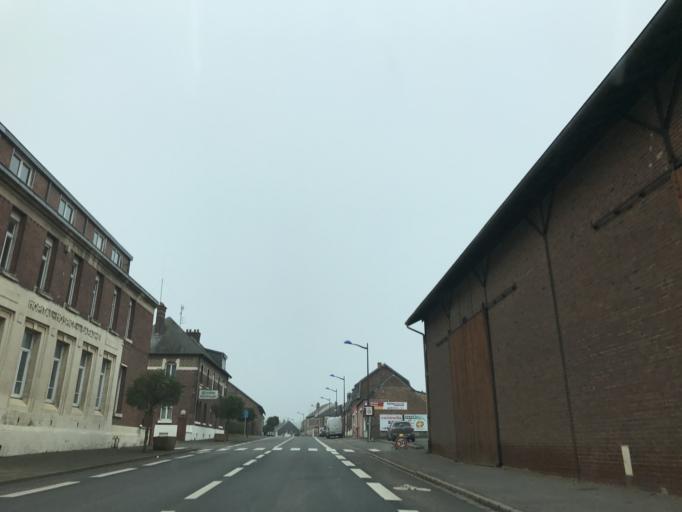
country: FR
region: Nord-Pas-de-Calais
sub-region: Departement du Pas-de-Calais
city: Bapaume
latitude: 50.1037
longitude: 2.8569
